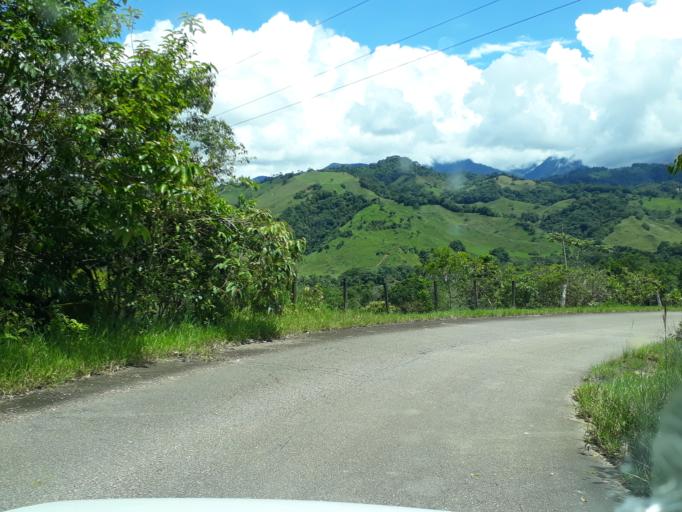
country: CO
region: Cundinamarca
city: Medina
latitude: 4.5767
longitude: -73.3233
